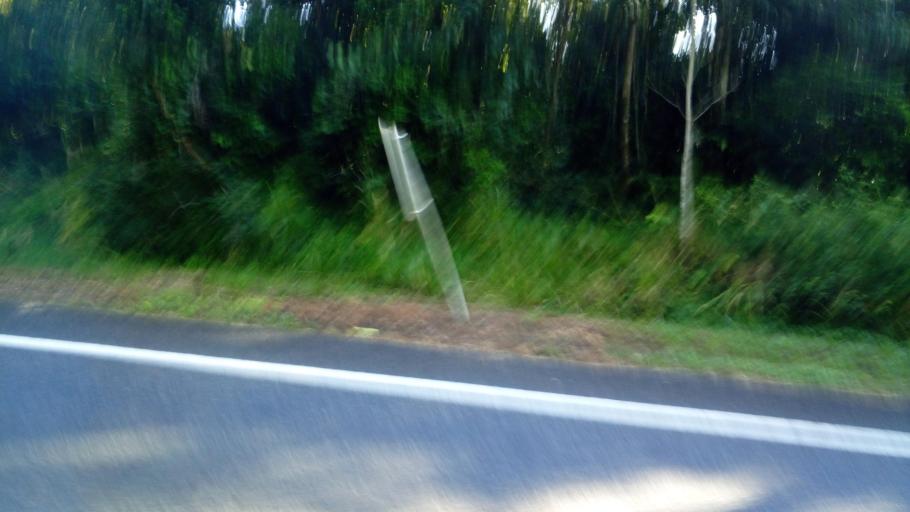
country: AU
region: Queensland
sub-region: Tablelands
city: Ravenshoe
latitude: -17.5950
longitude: 145.7464
